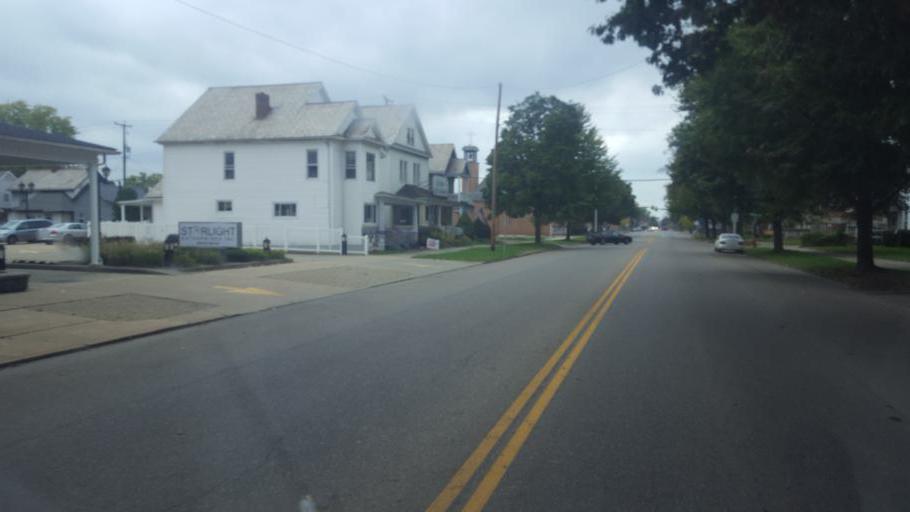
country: US
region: Ohio
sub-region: Tuscarawas County
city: New Philadelphia
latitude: 40.4890
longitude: -81.4415
